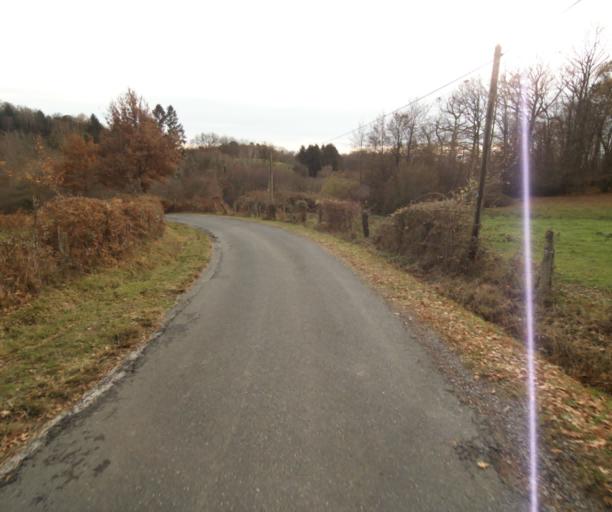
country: FR
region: Limousin
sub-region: Departement de la Correze
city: Saint-Mexant
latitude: 45.2602
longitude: 1.6472
